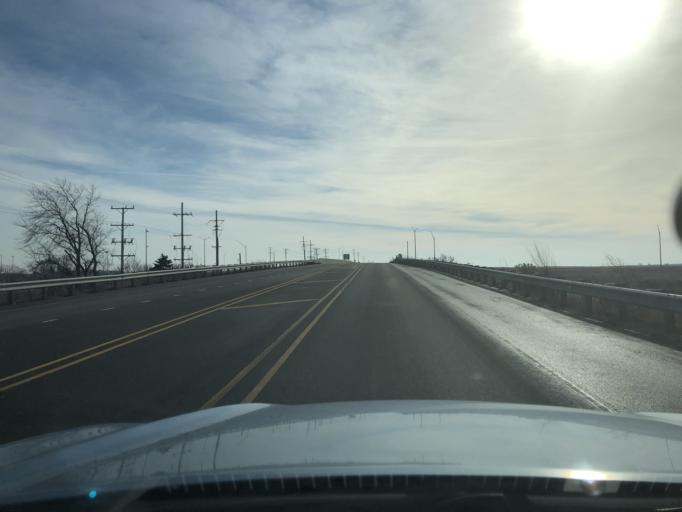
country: US
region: Illinois
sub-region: Boone County
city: Belvidere
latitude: 42.2350
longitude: -88.8191
